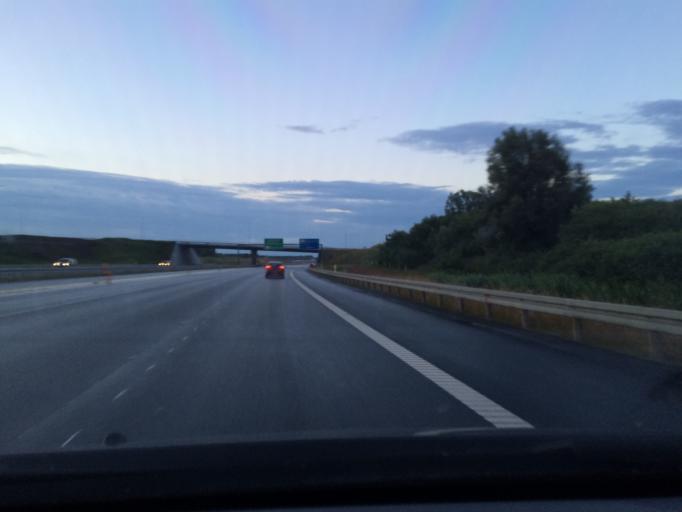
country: DK
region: Zealand
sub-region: Solrod Kommune
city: Solrod
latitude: 55.5341
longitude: 12.1988
